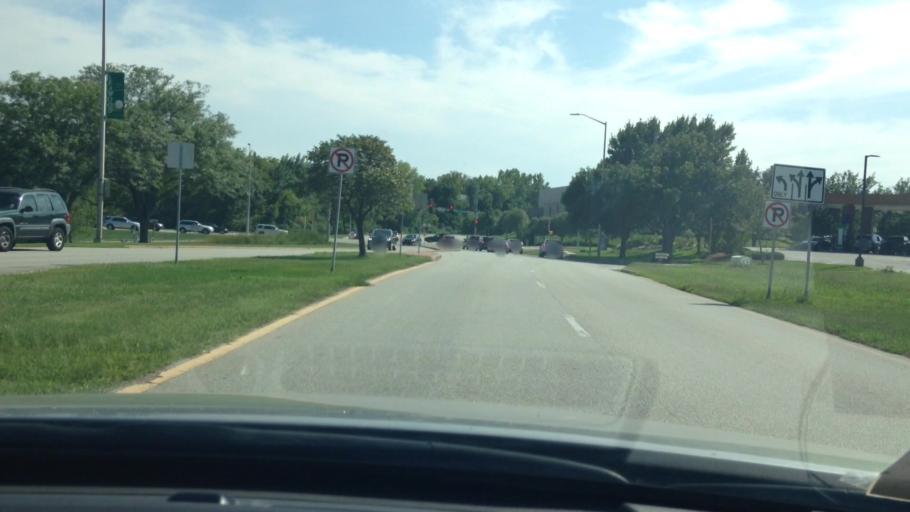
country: US
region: Kansas
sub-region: Johnson County
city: Leawood
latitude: 38.9142
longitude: -94.6349
